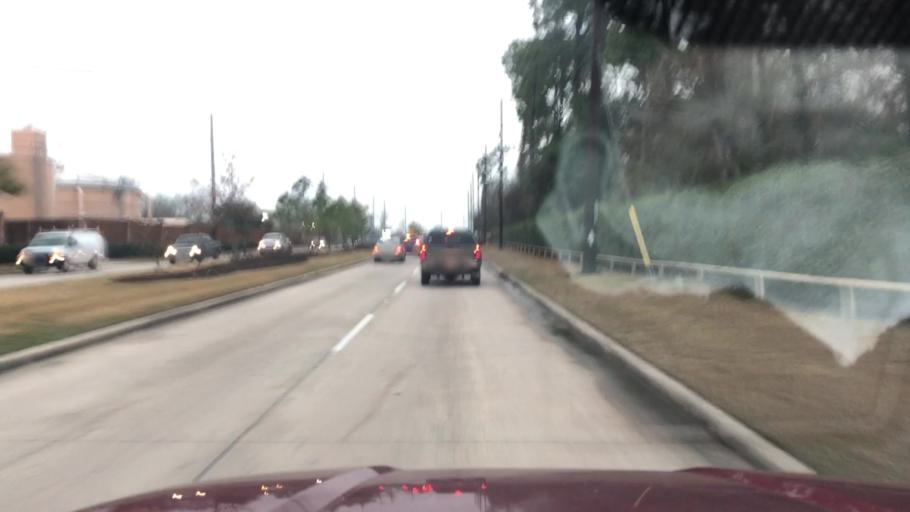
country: US
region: Texas
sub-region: Harris County
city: Tomball
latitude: 30.0380
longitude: -95.5366
